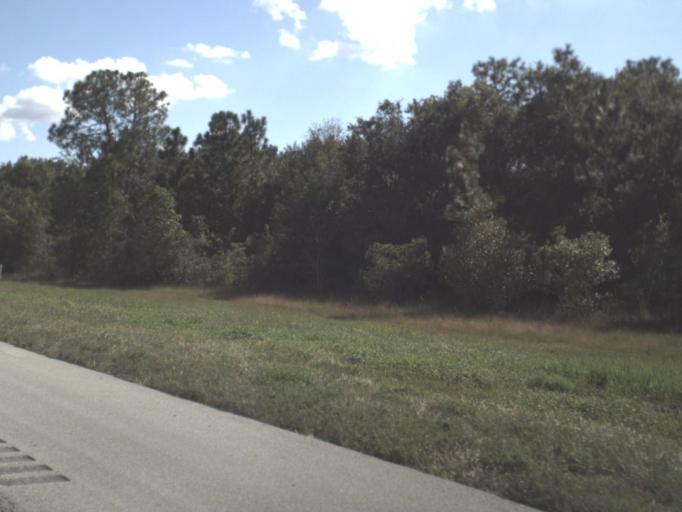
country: US
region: Florida
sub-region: Osceola County
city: Saint Cloud
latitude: 28.0137
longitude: -81.1716
